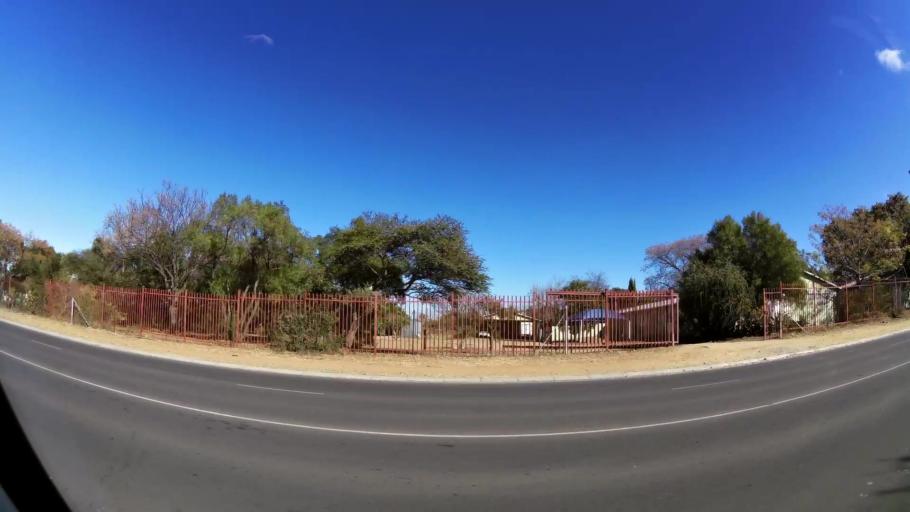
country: ZA
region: Limpopo
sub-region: Capricorn District Municipality
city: Polokwane
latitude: -23.9103
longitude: 29.4745
